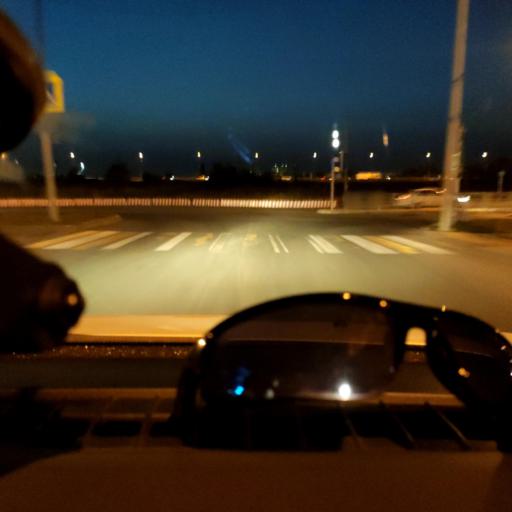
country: RU
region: Samara
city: Samara
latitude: 53.0984
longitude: 50.1633
